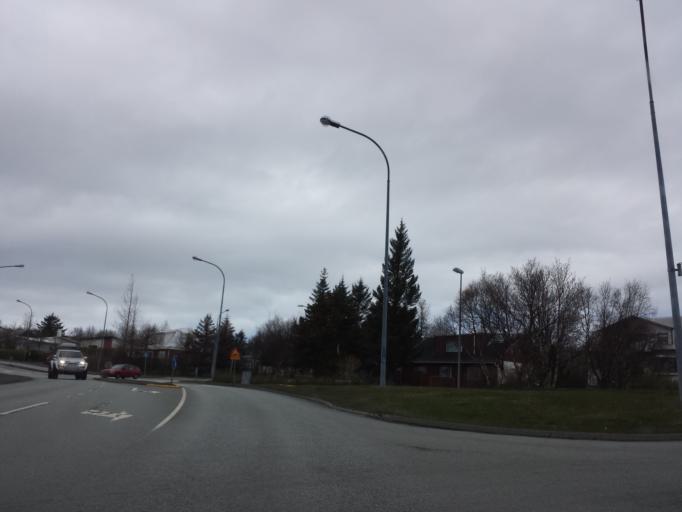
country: IS
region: Capital Region
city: Kopavogur
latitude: 64.1099
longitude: -21.8862
